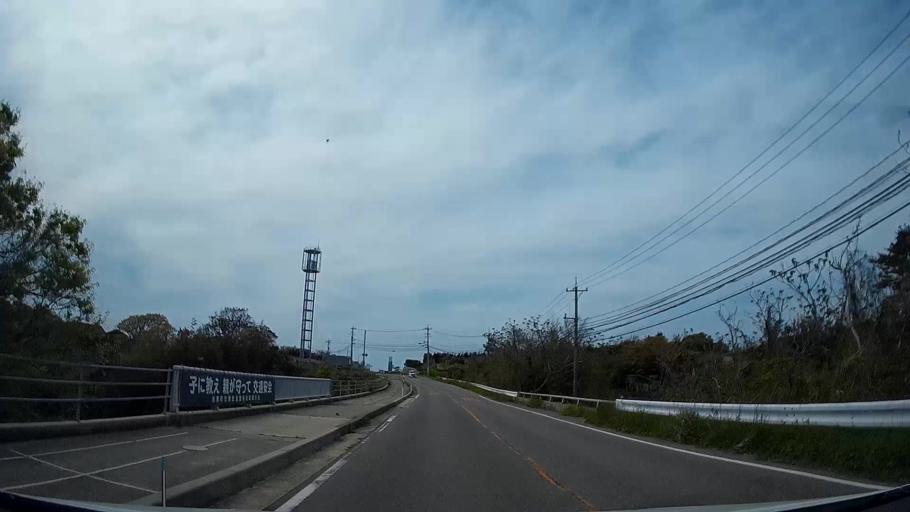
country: JP
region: Ishikawa
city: Hakui
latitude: 37.0527
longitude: 136.7314
